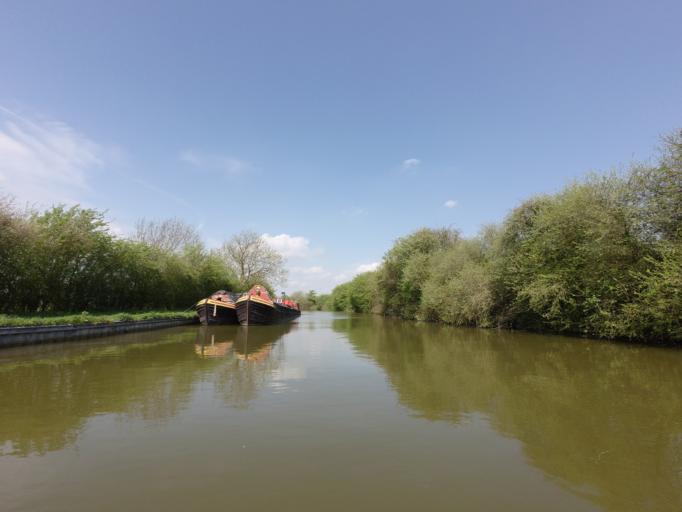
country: GB
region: England
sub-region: Buckinghamshire
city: Cheddington
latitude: 51.8750
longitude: -0.6556
